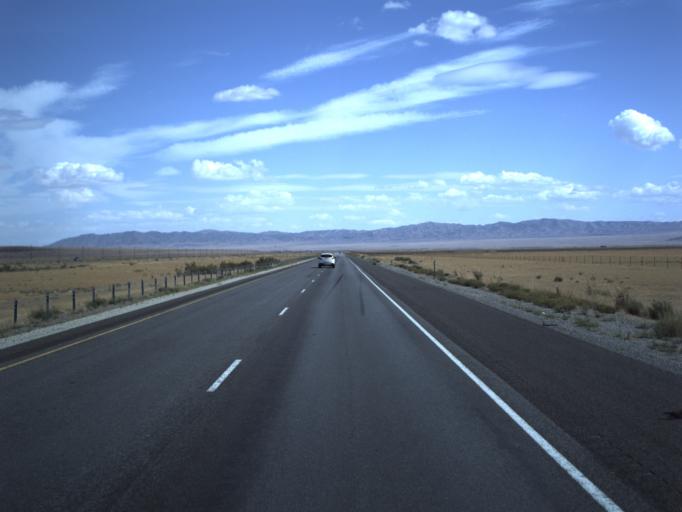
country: US
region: Utah
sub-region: Tooele County
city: Grantsville
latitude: 40.7257
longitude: -113.1976
